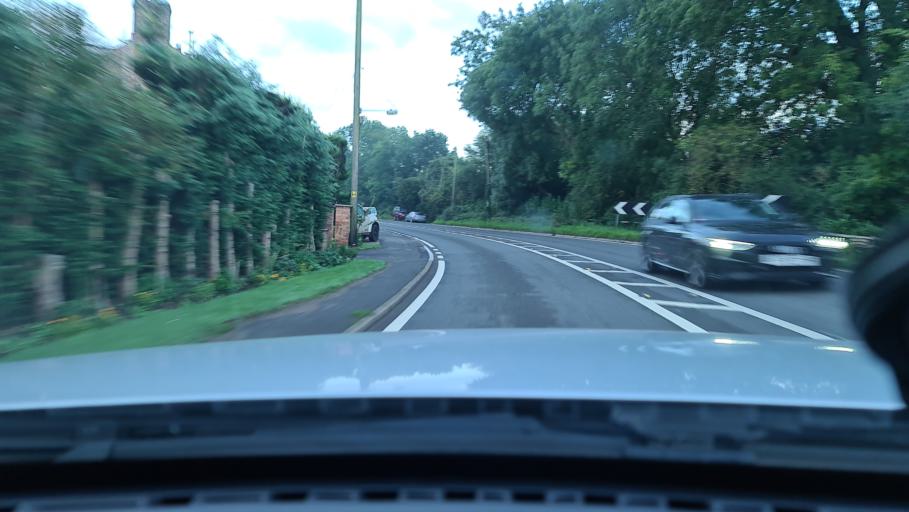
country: GB
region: England
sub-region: Warwickshire
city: Long Itchington
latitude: 52.2885
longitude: -1.3941
